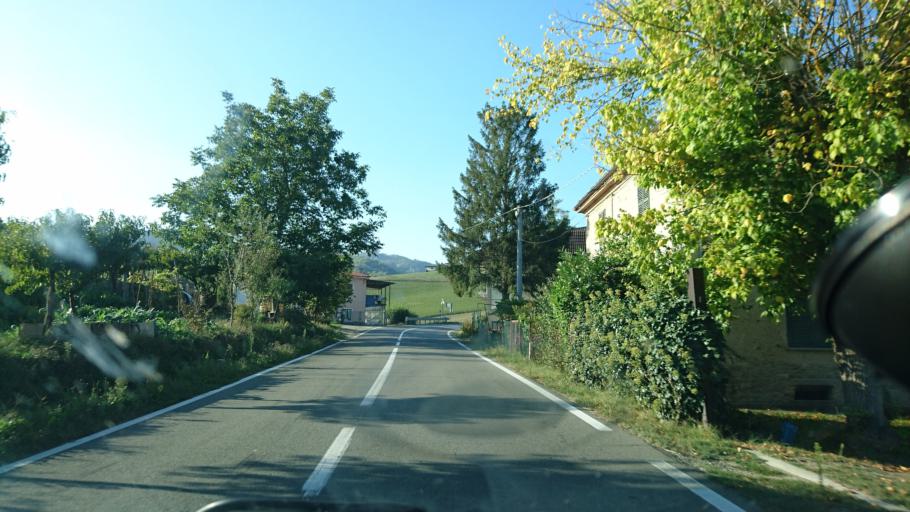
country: IT
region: Piedmont
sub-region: Provincia di Asti
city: Bubbio
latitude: 44.6658
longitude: 8.3008
